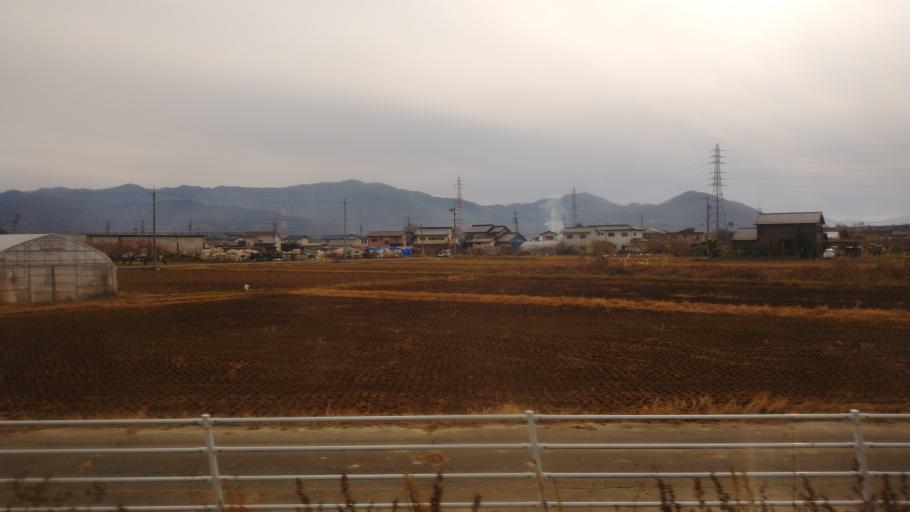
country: JP
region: Nagano
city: Nagano-shi
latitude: 36.5609
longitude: 138.1193
